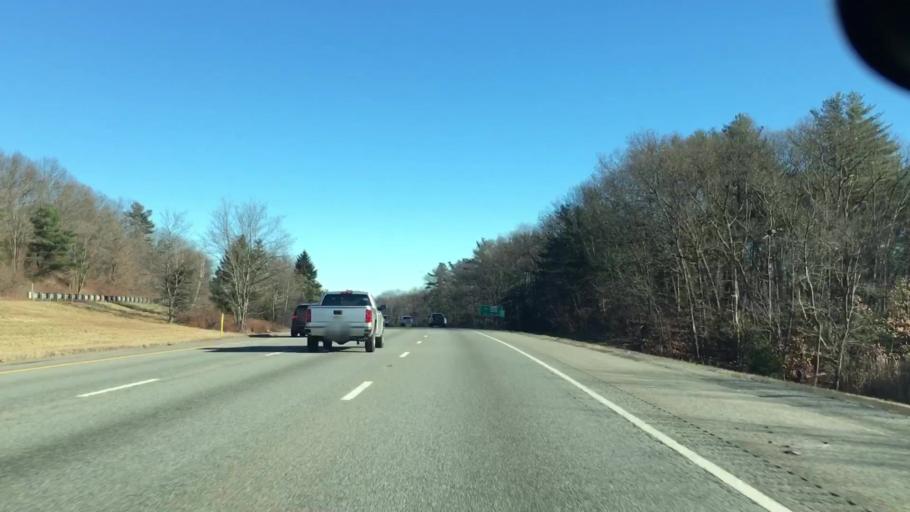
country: US
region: Massachusetts
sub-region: Middlesex County
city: Westford
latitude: 42.5577
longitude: -71.4421
